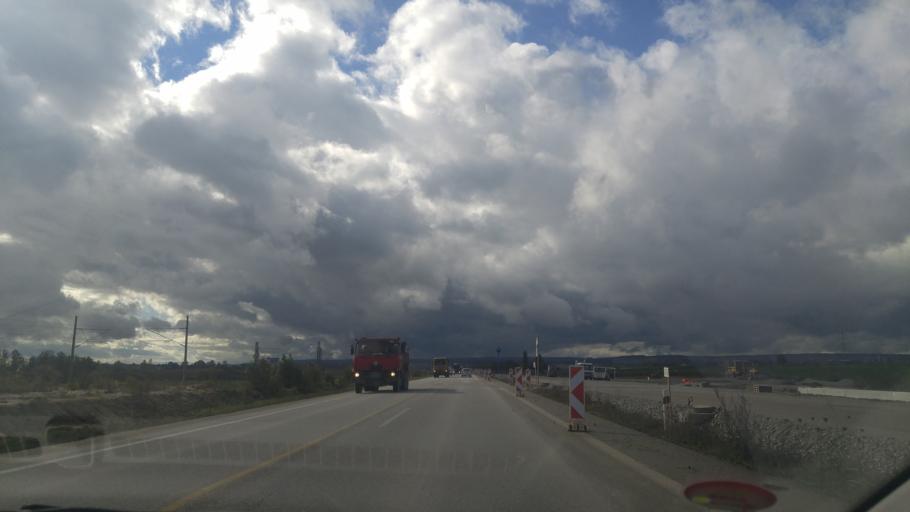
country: CZ
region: Jihocesky
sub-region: Okres Tabor
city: Veseli nad Luznici
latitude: 49.1647
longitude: 14.6576
